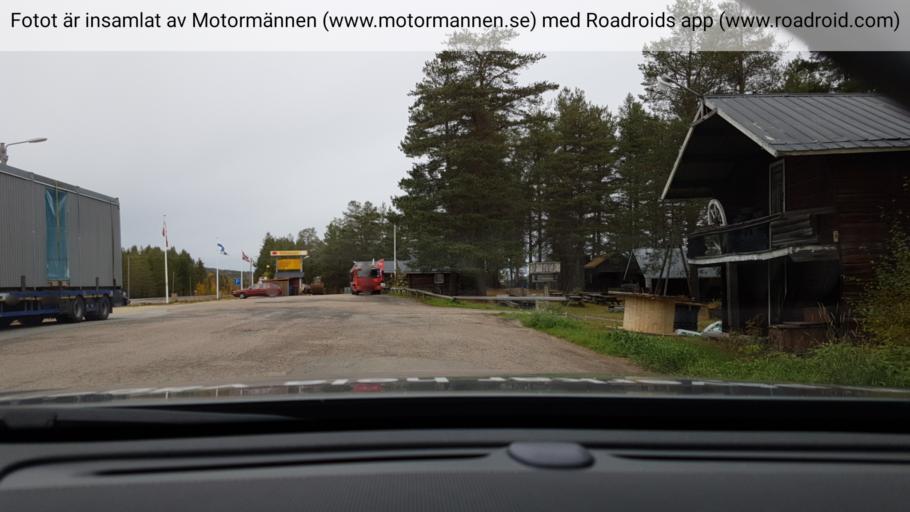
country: SE
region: Norrbotten
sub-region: Overkalix Kommun
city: OEverkalix
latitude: 66.2931
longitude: 22.8166
